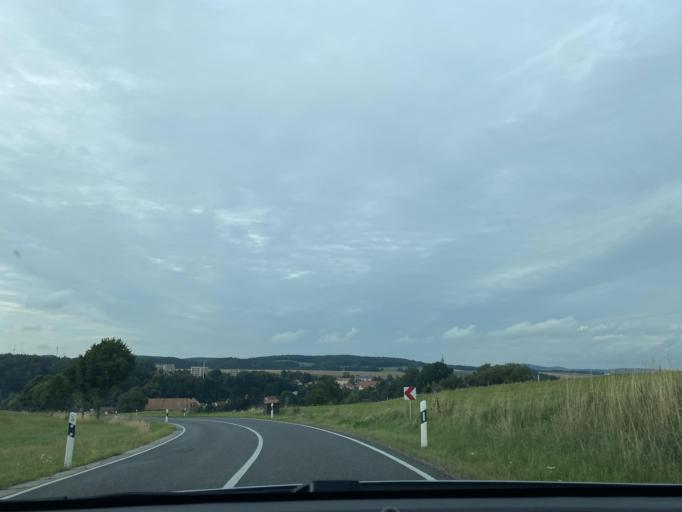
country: DE
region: Saxony
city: Bernstadt
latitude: 51.0417
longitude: 14.8199
